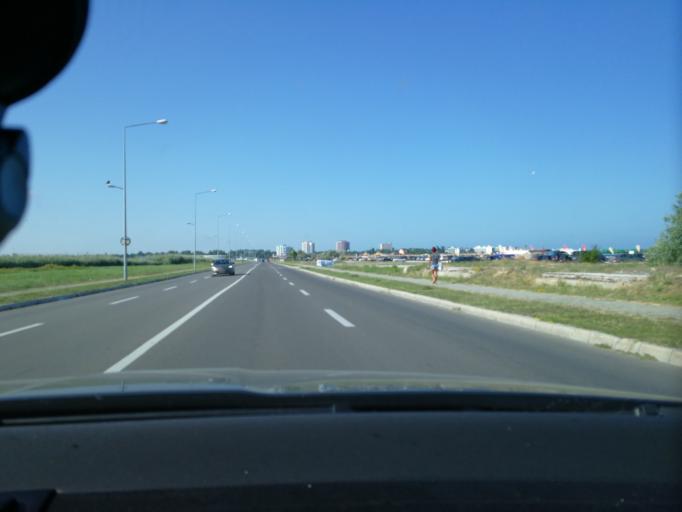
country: RO
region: Constanta
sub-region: Municipiul Mangalia
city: Mangalia
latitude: 43.8337
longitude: 28.5885
